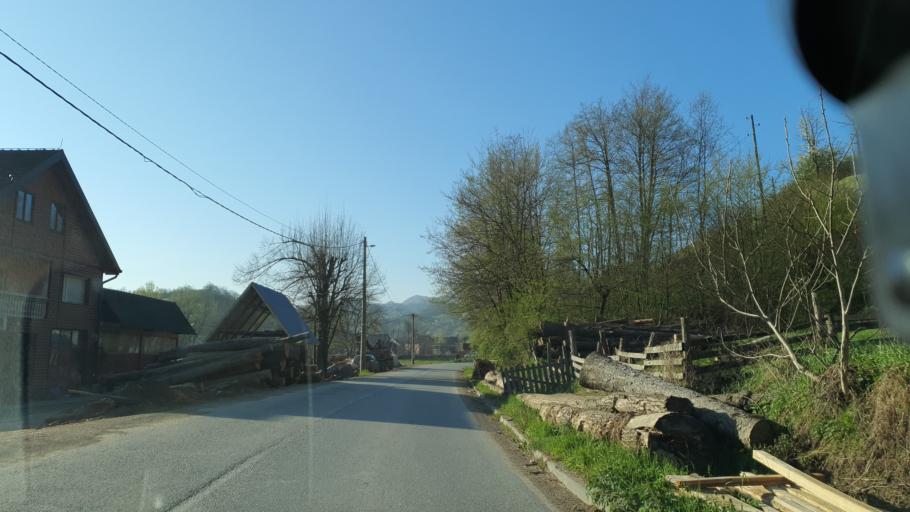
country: RS
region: Central Serbia
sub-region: Kolubarski Okrug
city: Osecina
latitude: 44.2976
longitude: 19.5358
